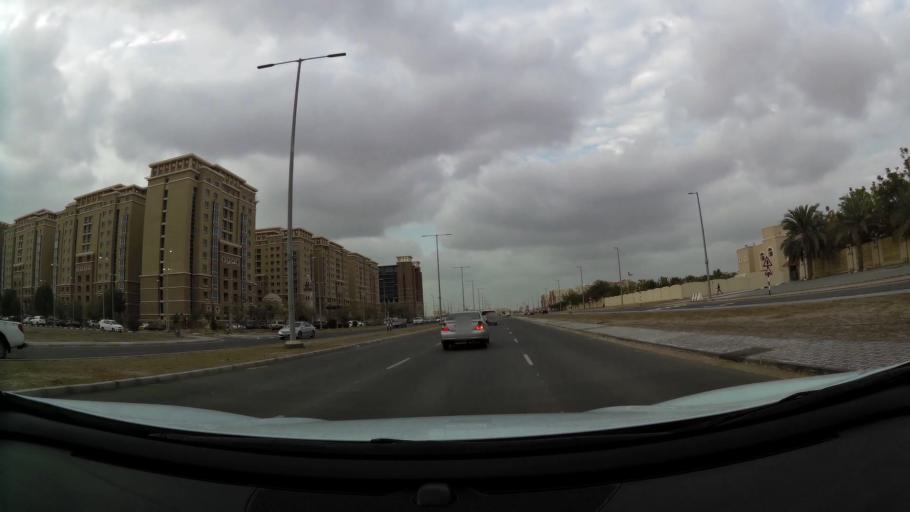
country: AE
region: Abu Dhabi
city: Abu Dhabi
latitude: 24.3696
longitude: 54.5398
